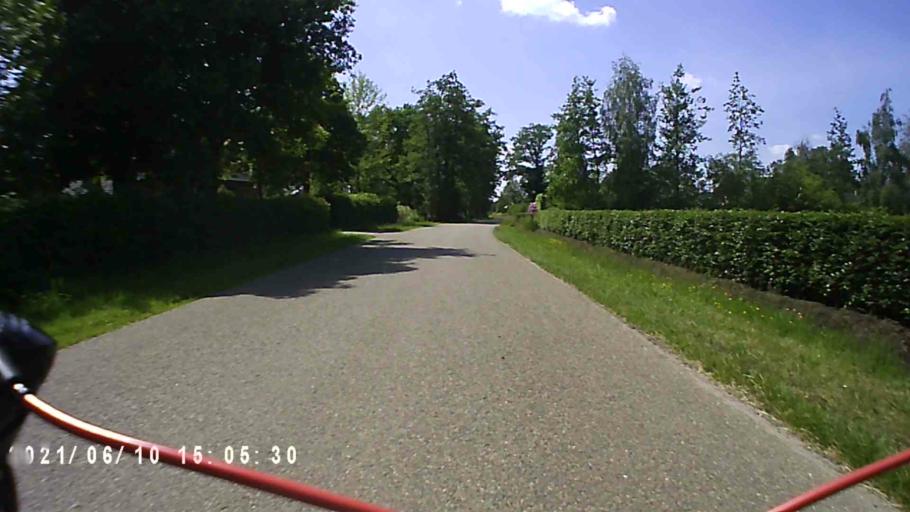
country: NL
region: Friesland
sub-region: Gemeente Achtkarspelen
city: Surhuizum
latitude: 53.1951
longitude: 6.2193
